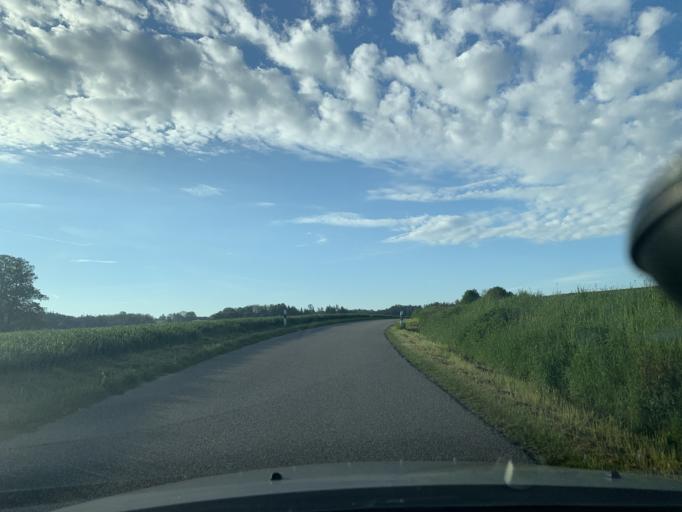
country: DE
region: Bavaria
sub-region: Lower Bavaria
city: Stallwang
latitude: 48.5258
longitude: 12.2075
